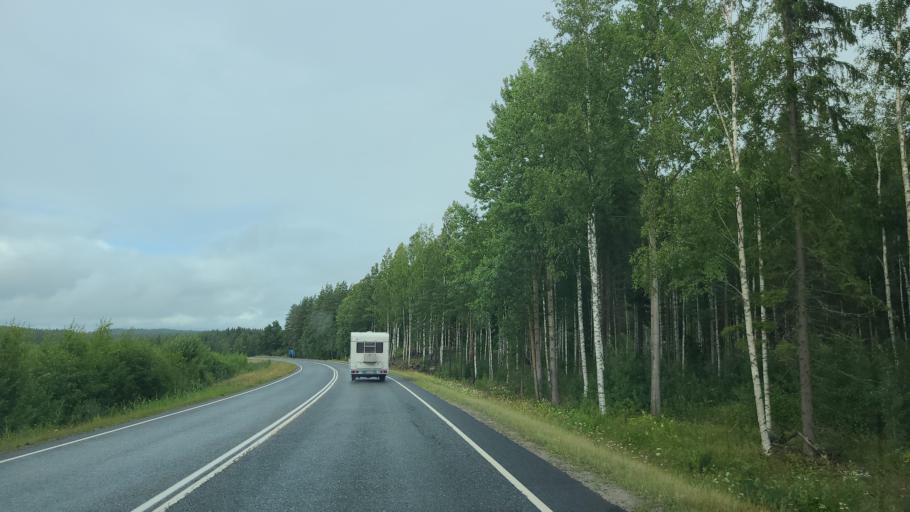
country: FI
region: Varsinais-Suomi
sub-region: Turku
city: Sauvo
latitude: 60.3254
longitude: 22.7137
